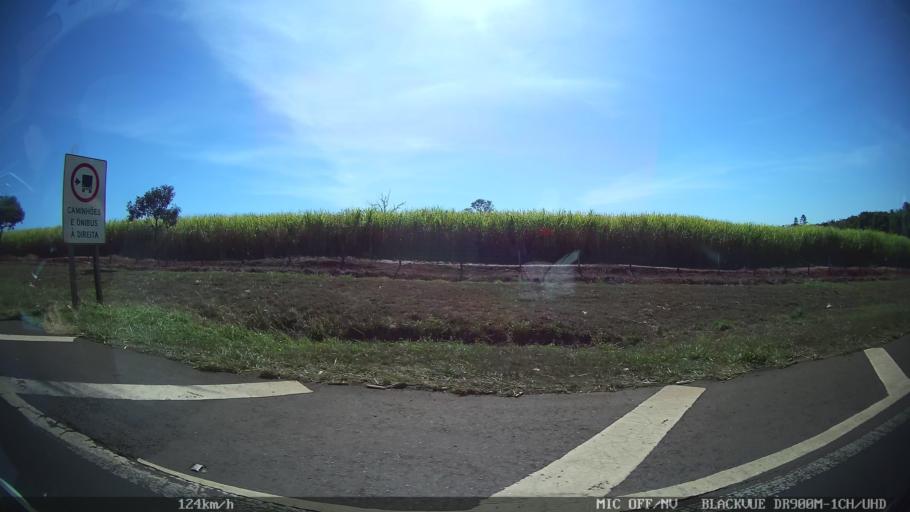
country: BR
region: Sao Paulo
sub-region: Barretos
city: Barretos
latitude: -20.5612
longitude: -48.6533
